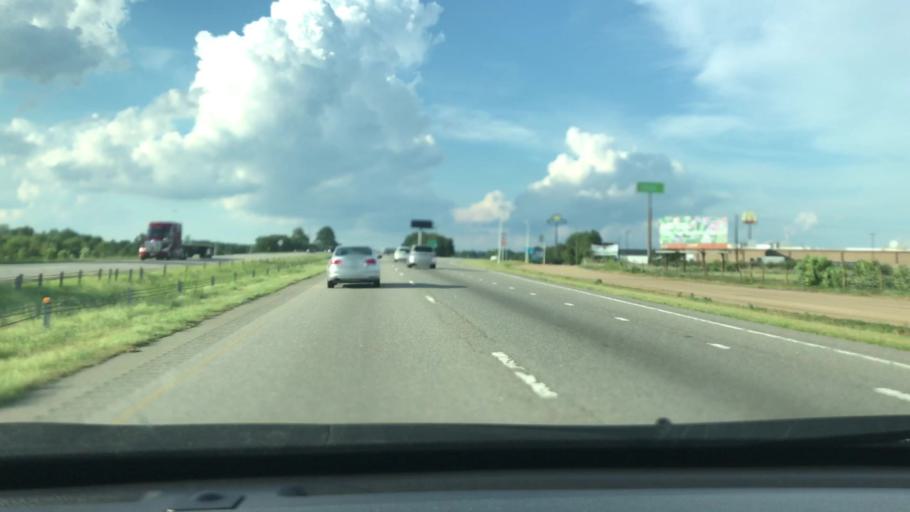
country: US
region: North Carolina
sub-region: Robeson County
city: Saint Pauls
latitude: 34.8069
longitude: -78.9880
